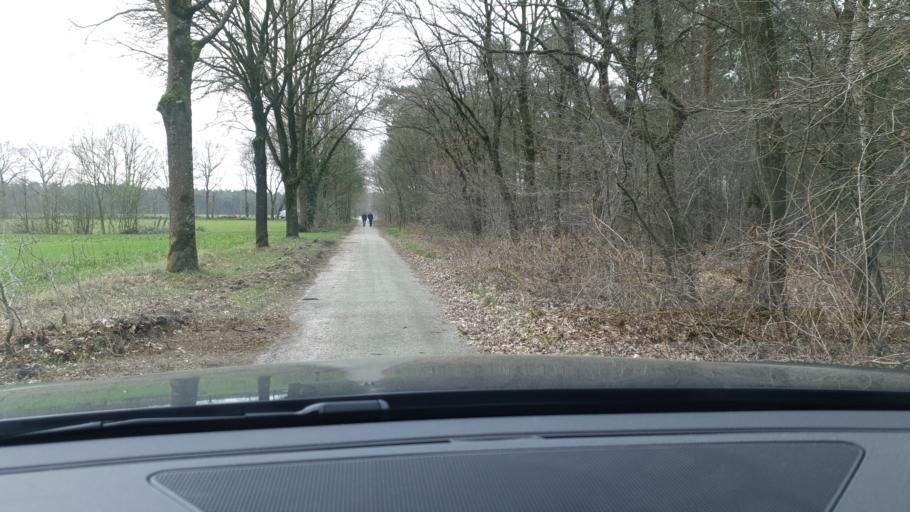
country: NL
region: North Brabant
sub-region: Gemeente Oirschot
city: Middelbeers
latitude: 51.4283
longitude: 5.2658
